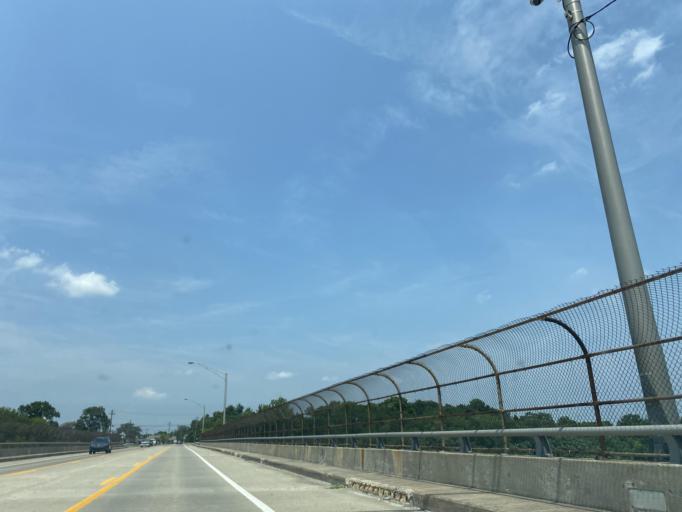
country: US
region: Kentucky
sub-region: Campbell County
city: Highland Heights
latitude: 39.0495
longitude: -84.4465
